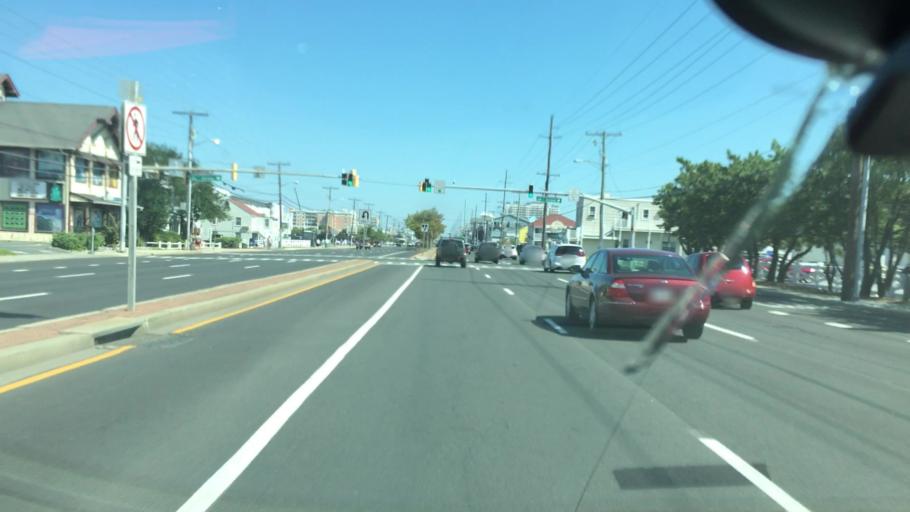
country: US
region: Maryland
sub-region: Worcester County
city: Ocean City
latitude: 38.3634
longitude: -75.0724
